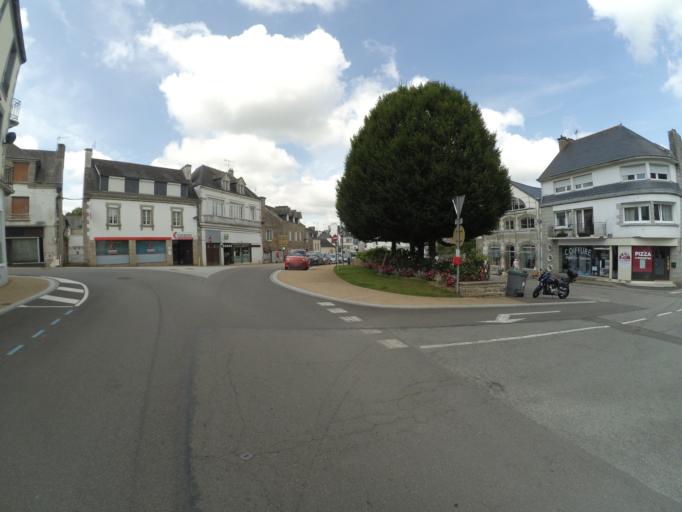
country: FR
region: Brittany
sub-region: Departement du Finistere
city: Rosporden
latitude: 47.9582
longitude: -3.8287
